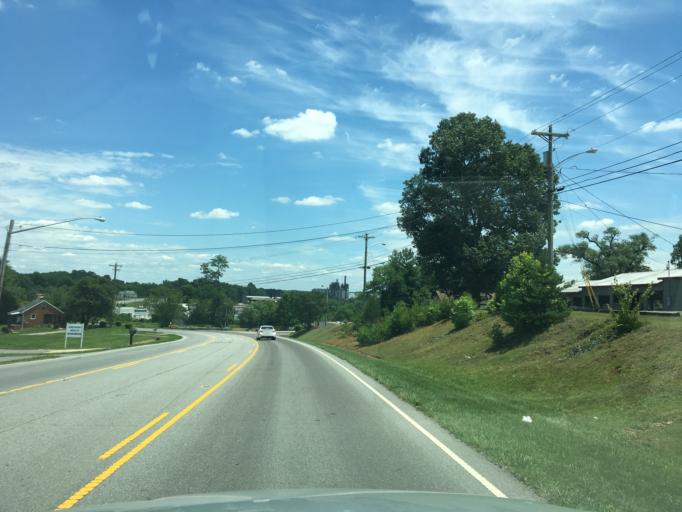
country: US
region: North Carolina
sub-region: Burke County
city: Glen Alpine
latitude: 35.7268
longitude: -81.7394
